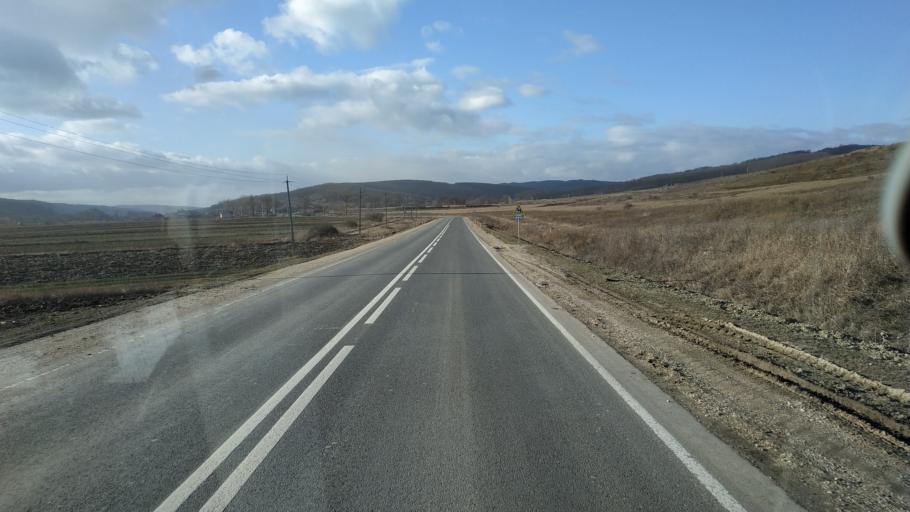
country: MD
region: Calarasi
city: Calarasi
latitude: 47.3248
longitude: 28.1035
